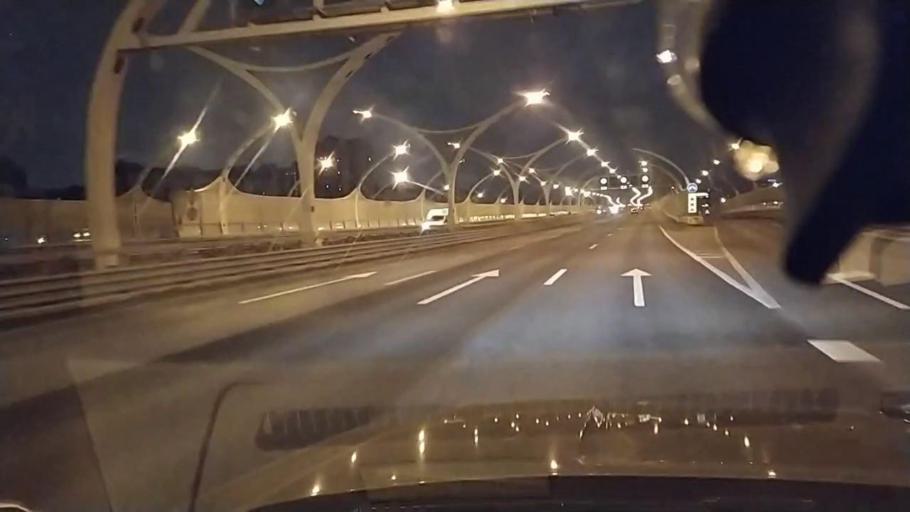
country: RU
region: St.-Petersburg
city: Staraya Derevnya
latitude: 60.0076
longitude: 30.2336
